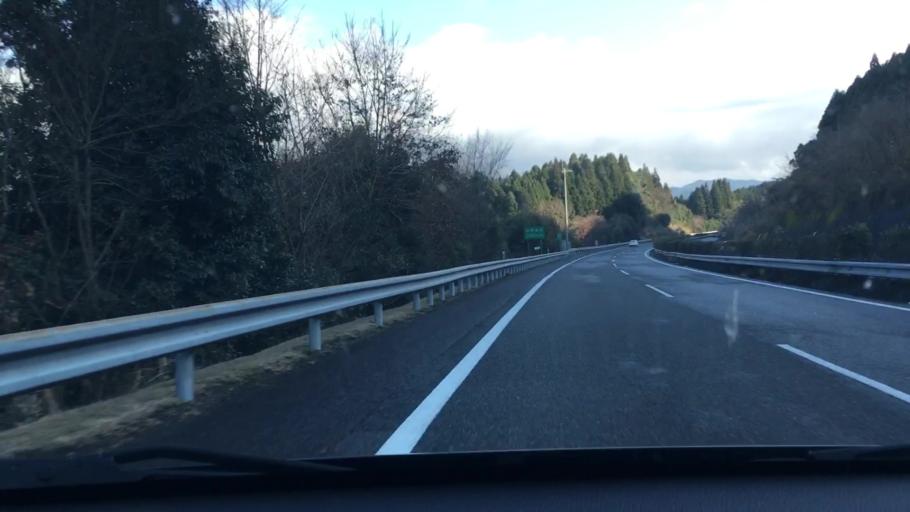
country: JP
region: Kumamoto
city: Hitoyoshi
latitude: 32.1784
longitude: 130.7872
